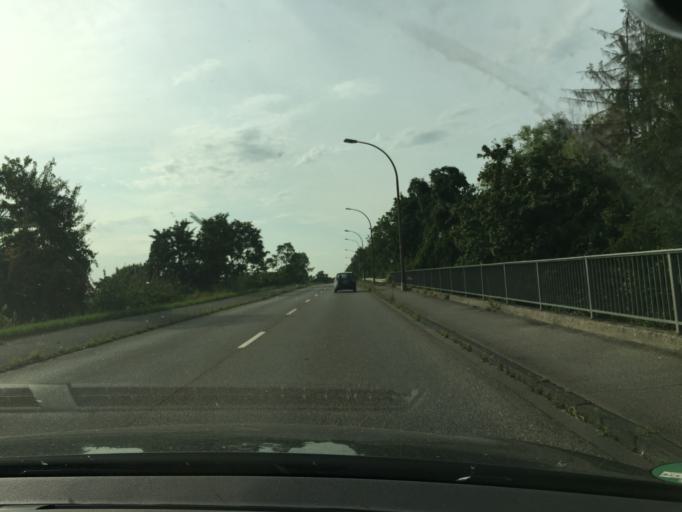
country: DE
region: North Rhine-Westphalia
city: Wesseling
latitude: 50.8169
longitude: 6.9937
